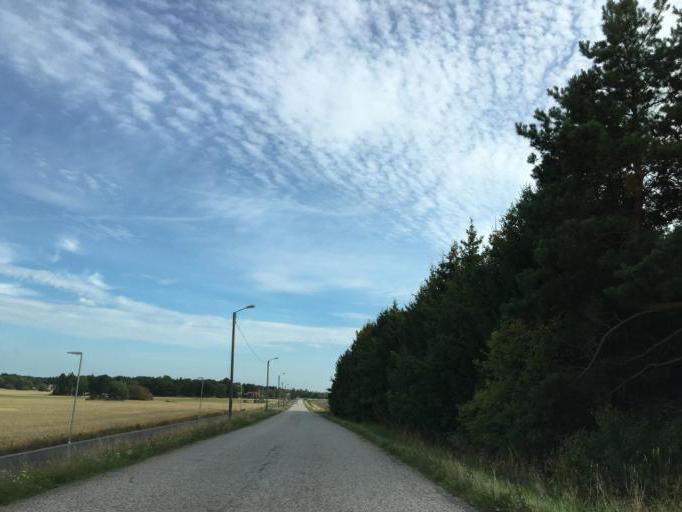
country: SE
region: Soedermanland
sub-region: Eskilstuna Kommun
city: Torshalla
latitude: 59.4449
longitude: 16.4694
